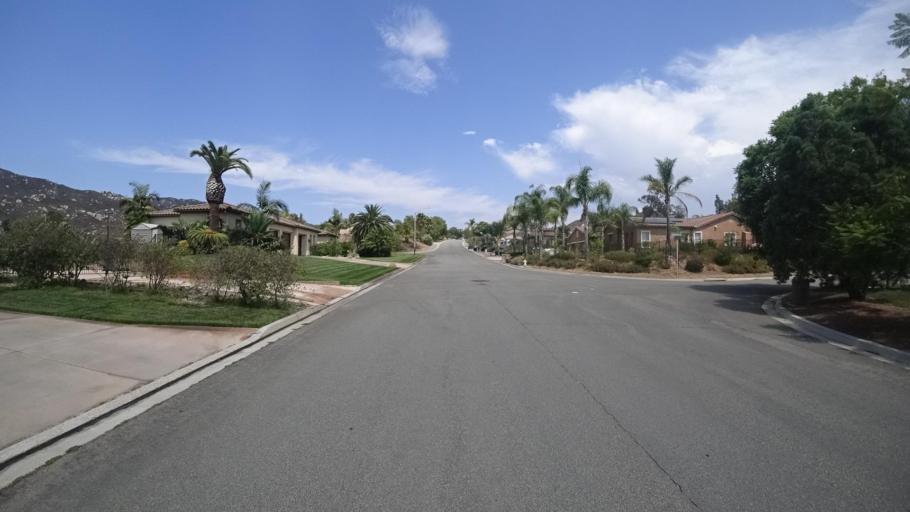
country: US
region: California
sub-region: San Diego County
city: Hidden Meadows
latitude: 33.1828
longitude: -117.0917
